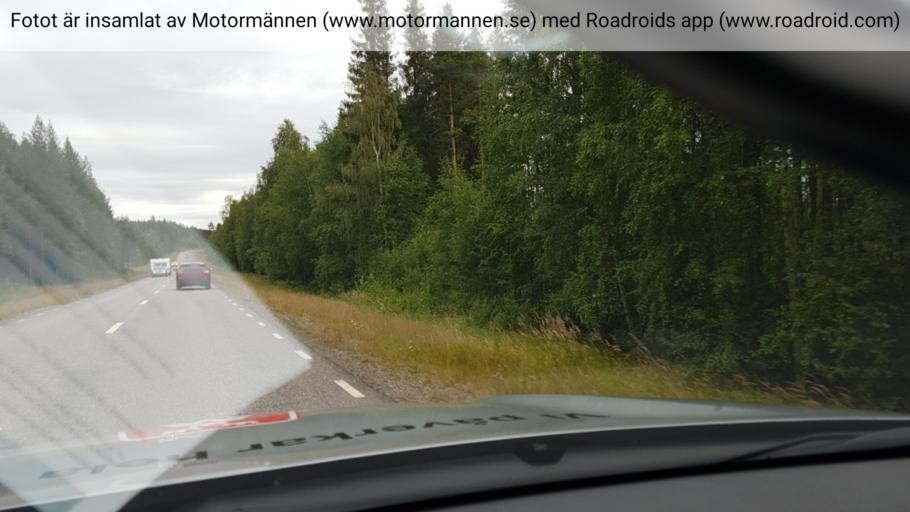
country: SE
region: Norrbotten
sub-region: Overkalix Kommun
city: OEverkalix
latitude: 66.5252
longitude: 22.7598
